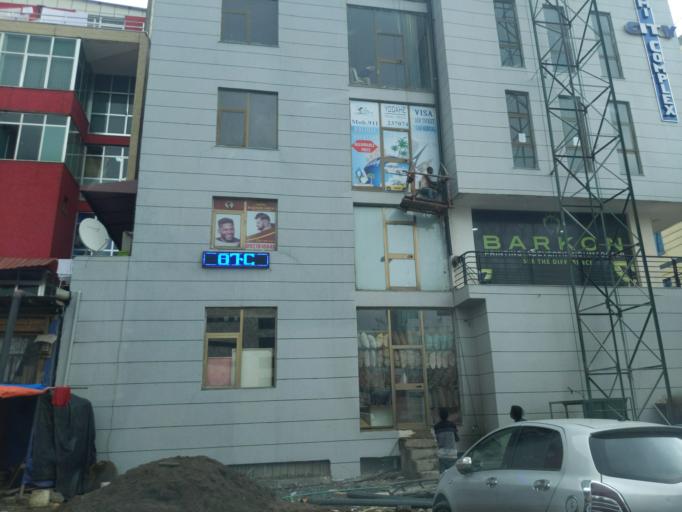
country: ET
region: Adis Abeba
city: Addis Ababa
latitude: 8.9960
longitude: 38.7871
